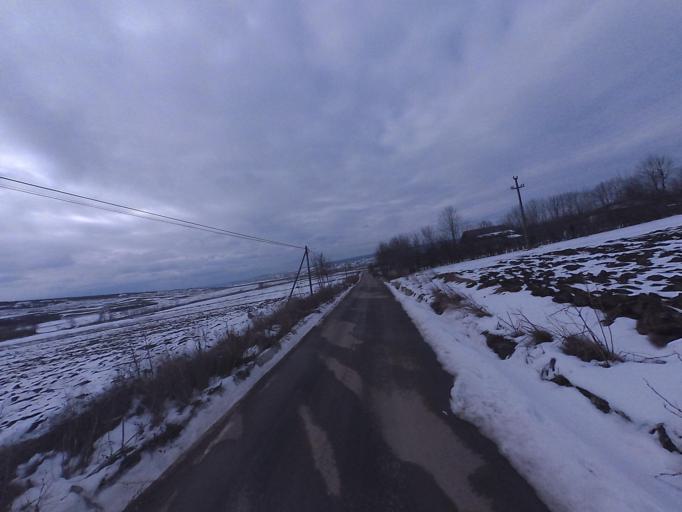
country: RO
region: Iasi
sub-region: Comuna Tibana
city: Tibana
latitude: 46.9832
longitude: 27.3514
